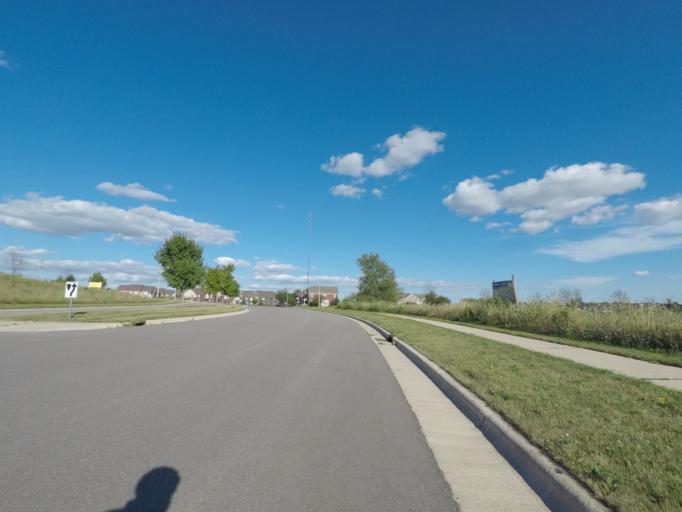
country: US
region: Wisconsin
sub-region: Dane County
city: Middleton
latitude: 43.0577
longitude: -89.5536
